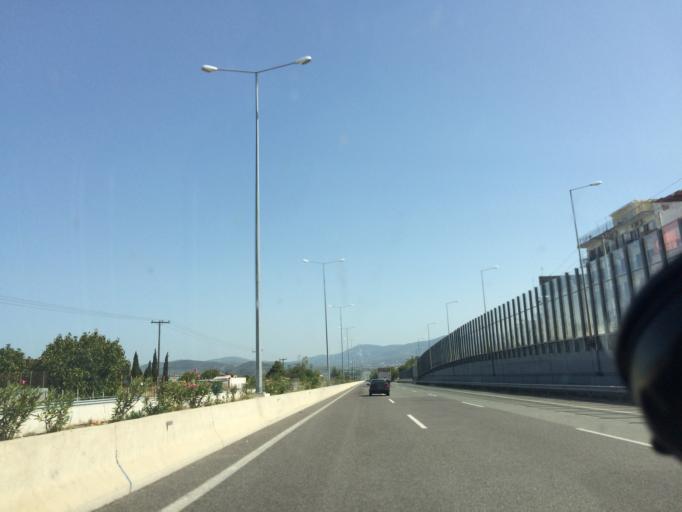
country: GR
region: Central Greece
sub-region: Nomos Voiotias
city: Oinofyta
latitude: 38.3120
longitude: 23.6373
